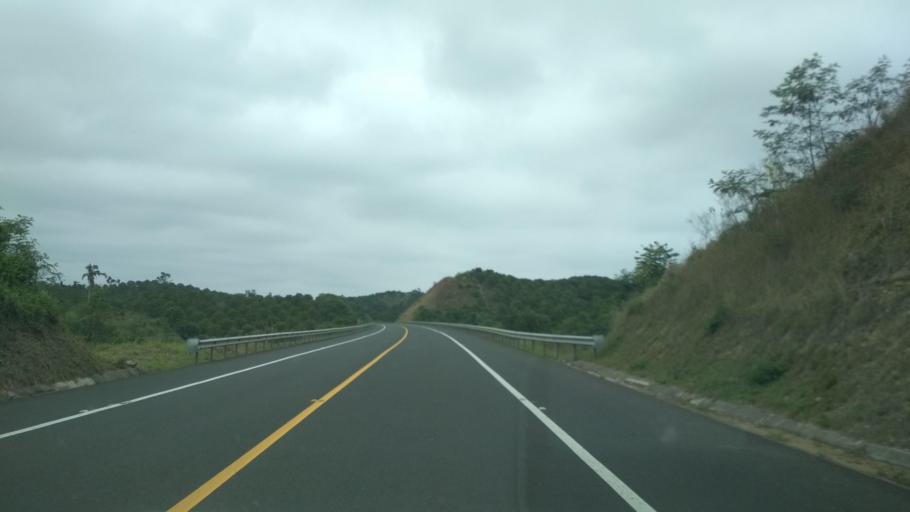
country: MX
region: Veracruz
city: Gutierrez Zamora
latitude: 20.2958
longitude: -97.0777
